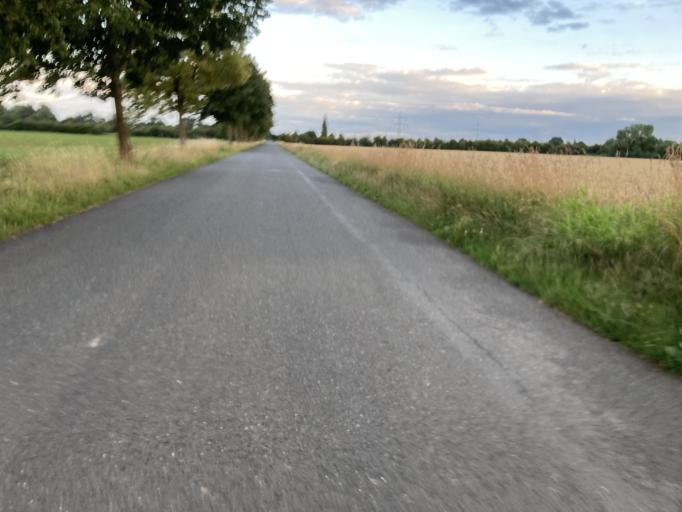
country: DE
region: Lower Saxony
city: Verden
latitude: 52.9285
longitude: 9.2004
